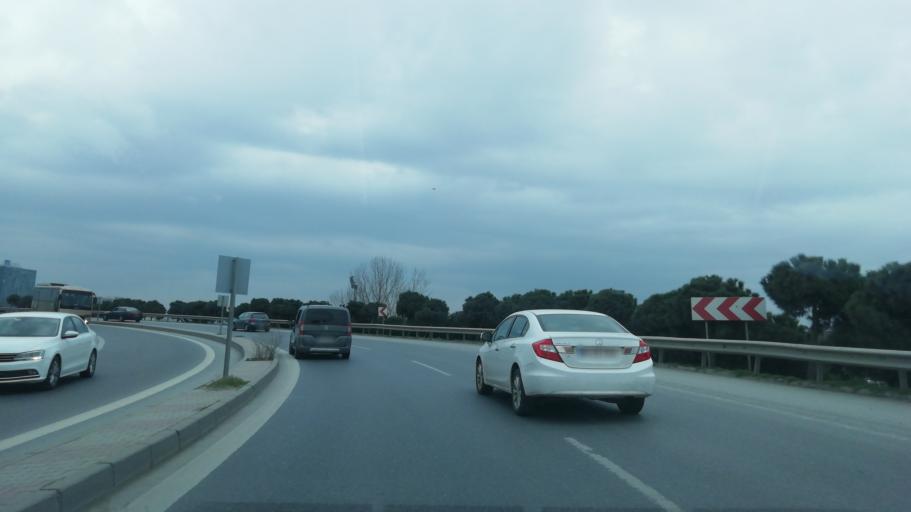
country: TR
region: Istanbul
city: Bahcelievler
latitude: 40.9994
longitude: 28.8164
